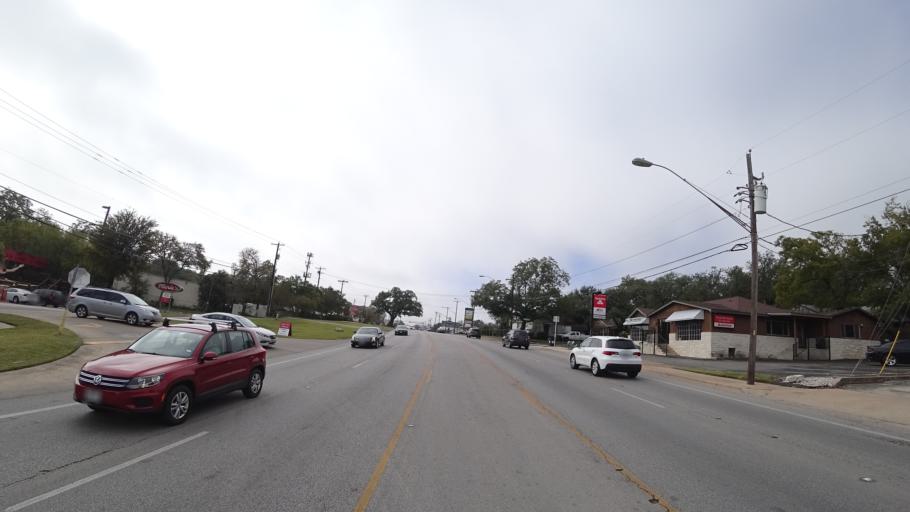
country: US
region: Texas
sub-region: Travis County
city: Rollingwood
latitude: 30.2464
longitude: -97.7783
